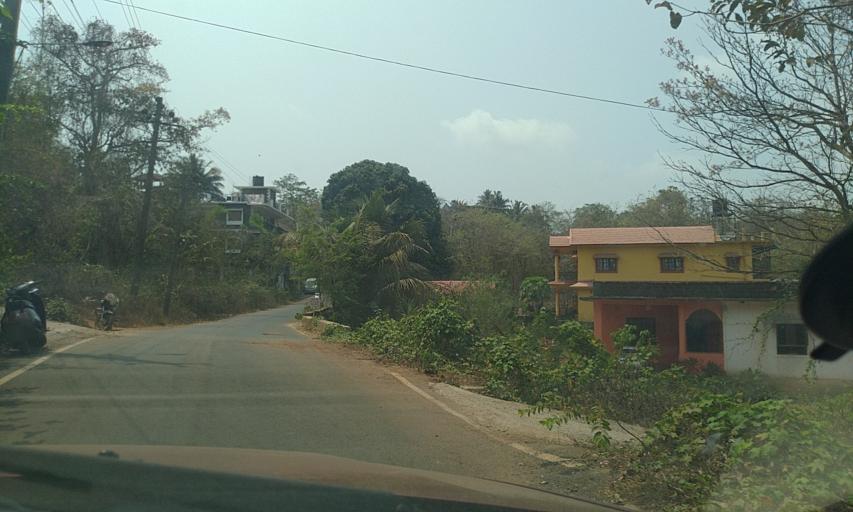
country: IN
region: Goa
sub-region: North Goa
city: Serula
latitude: 15.5246
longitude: 73.8390
